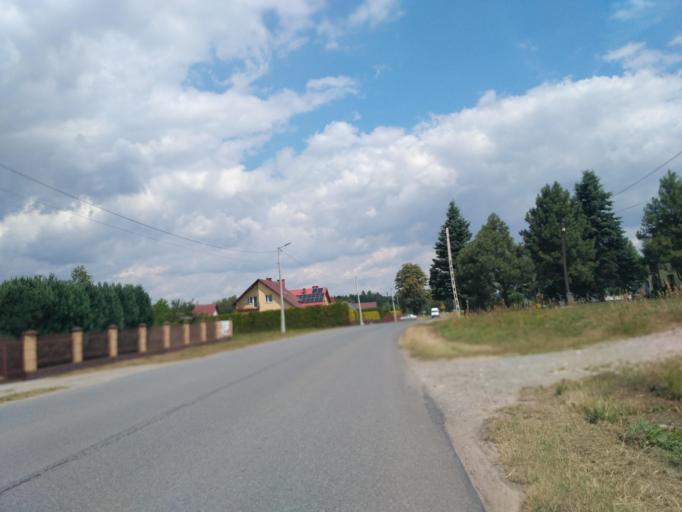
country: PL
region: Subcarpathian Voivodeship
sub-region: Powiat debicki
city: Pilzno
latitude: 50.0145
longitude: 21.2893
